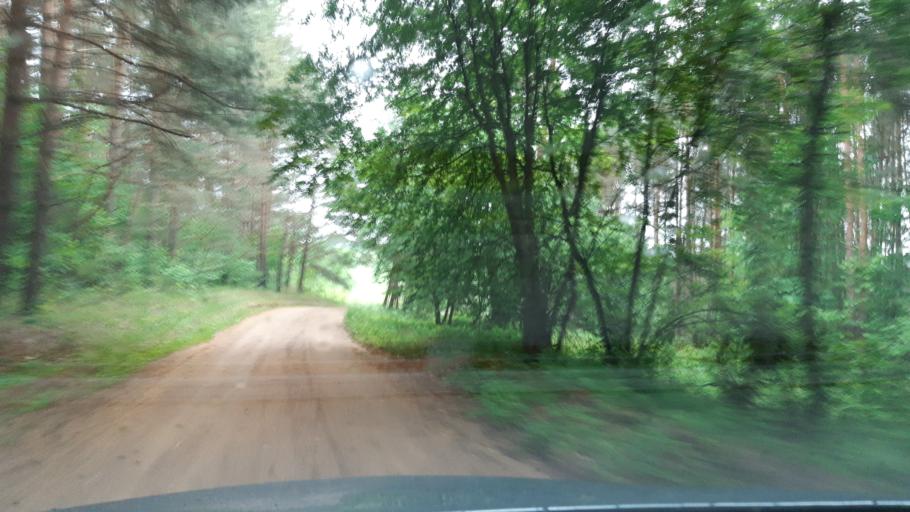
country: LT
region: Utenos apskritis
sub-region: Anyksciai
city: Anyksciai
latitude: 55.4477
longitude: 25.2080
